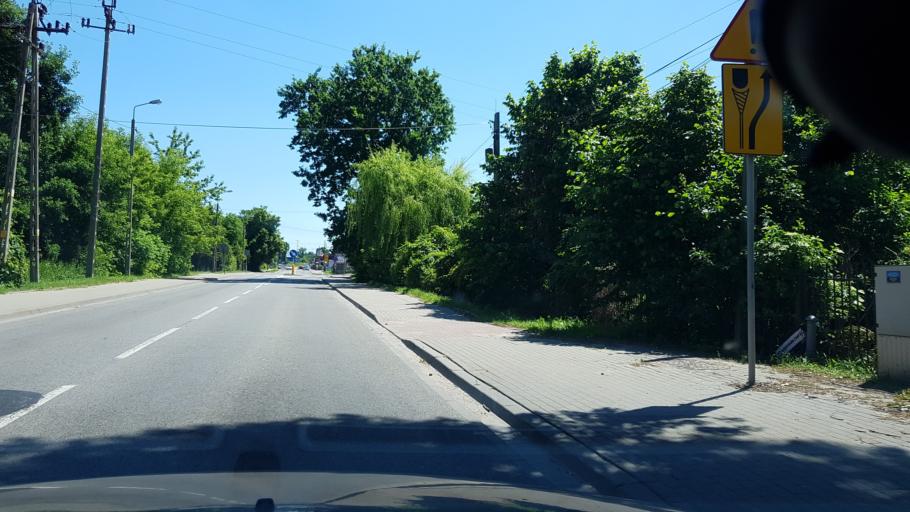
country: PL
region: Masovian Voivodeship
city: Zielonka
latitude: 52.3120
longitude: 21.1334
